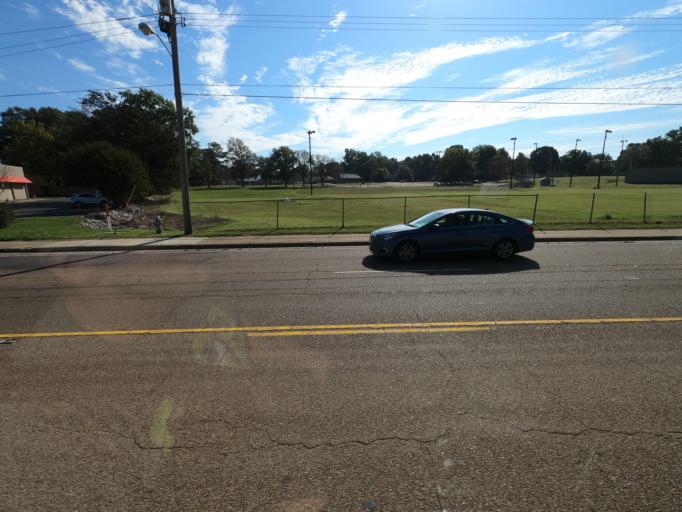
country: US
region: Tennessee
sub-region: Shelby County
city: Millington
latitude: 35.3532
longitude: -89.8974
